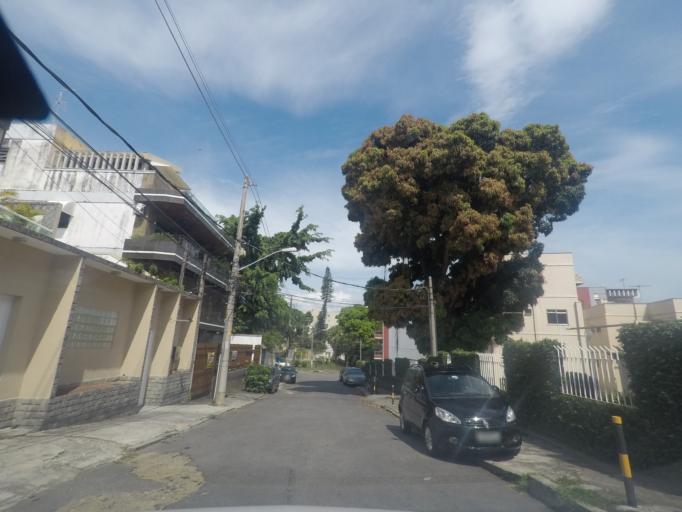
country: BR
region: Rio de Janeiro
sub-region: Rio De Janeiro
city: Rio de Janeiro
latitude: -22.8186
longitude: -43.1923
